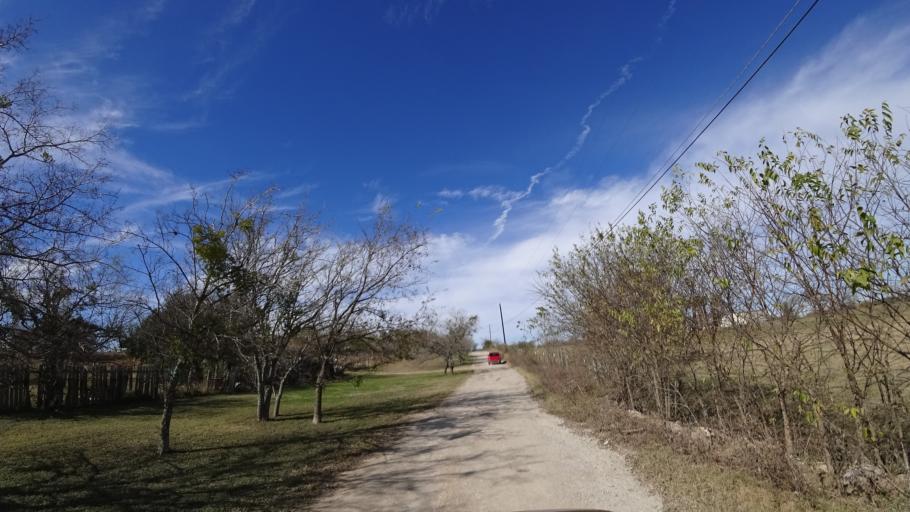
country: US
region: Texas
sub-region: Travis County
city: Onion Creek
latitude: 30.1185
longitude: -97.6881
